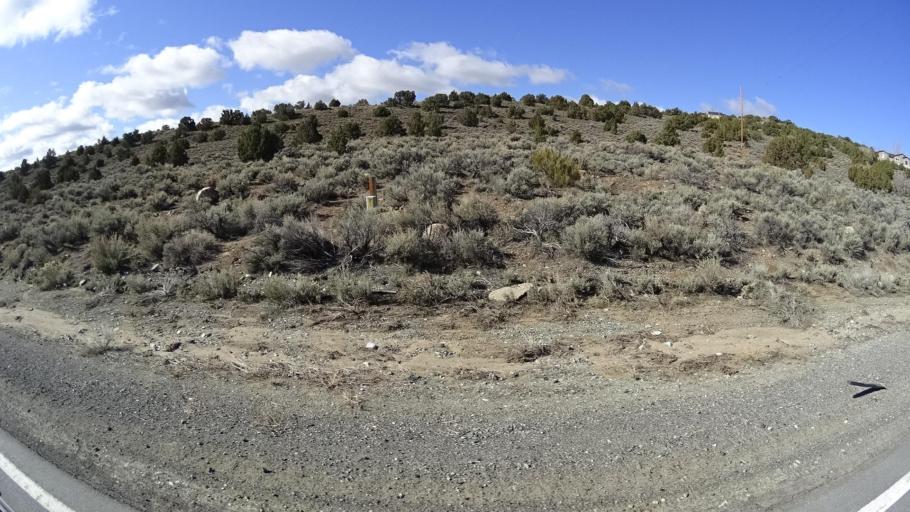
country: US
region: Nevada
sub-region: Washoe County
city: Lemmon Valley
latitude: 39.7352
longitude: -119.8832
